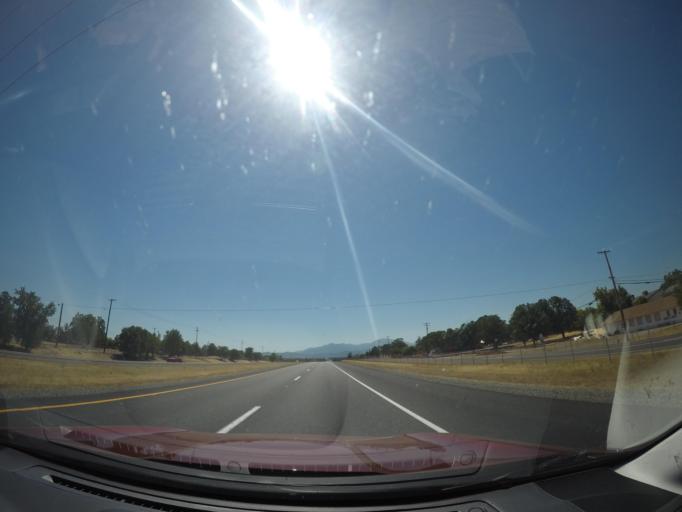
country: US
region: California
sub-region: Shasta County
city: Redding
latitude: 40.6176
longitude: -122.3345
